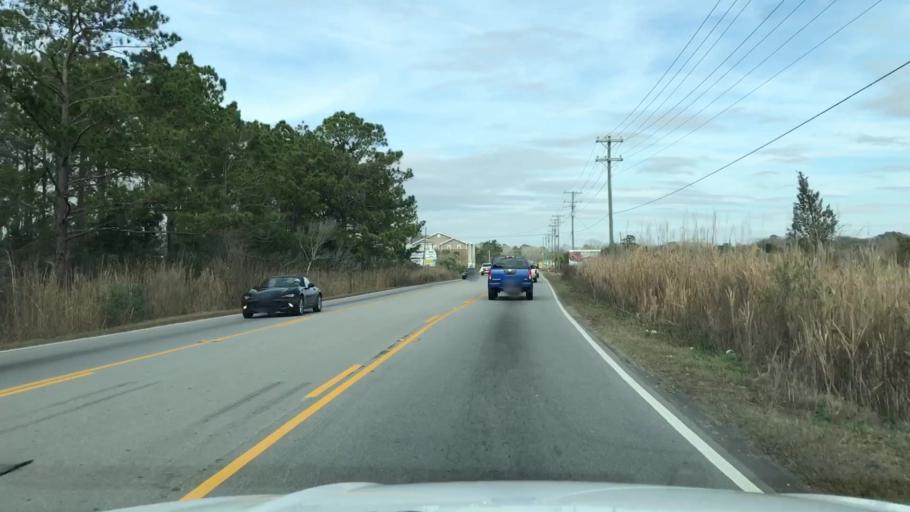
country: US
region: South Carolina
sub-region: Charleston County
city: Shell Point
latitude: 32.7971
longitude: -80.1085
